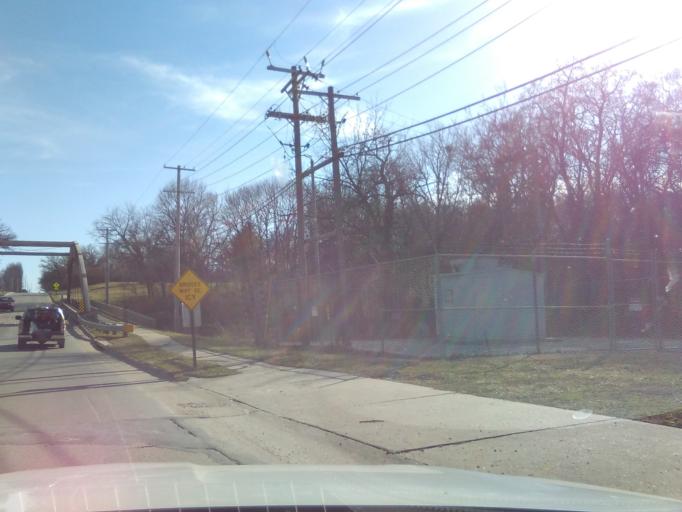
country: US
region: Nebraska
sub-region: Otoe County
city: Nebraska City
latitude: 40.6769
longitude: -95.8783
